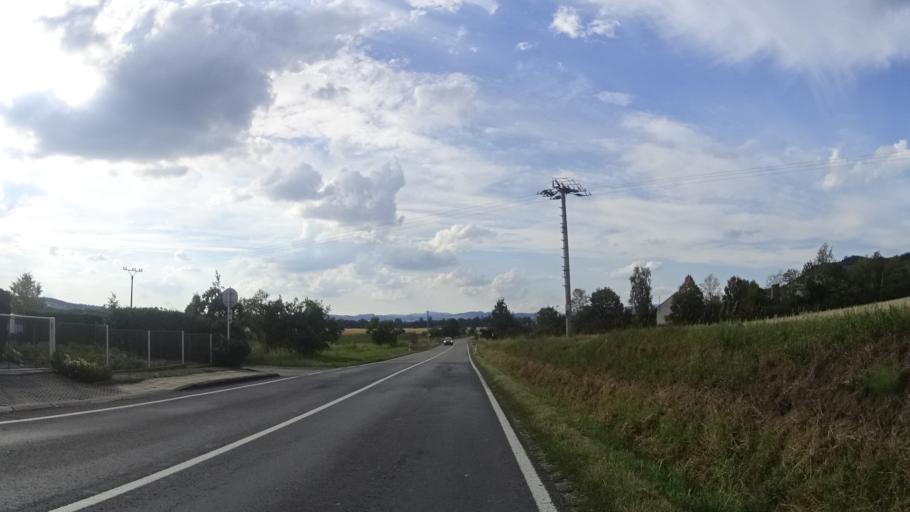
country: CZ
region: Olomoucky
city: Dubicko
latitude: 49.8460
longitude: 16.9502
